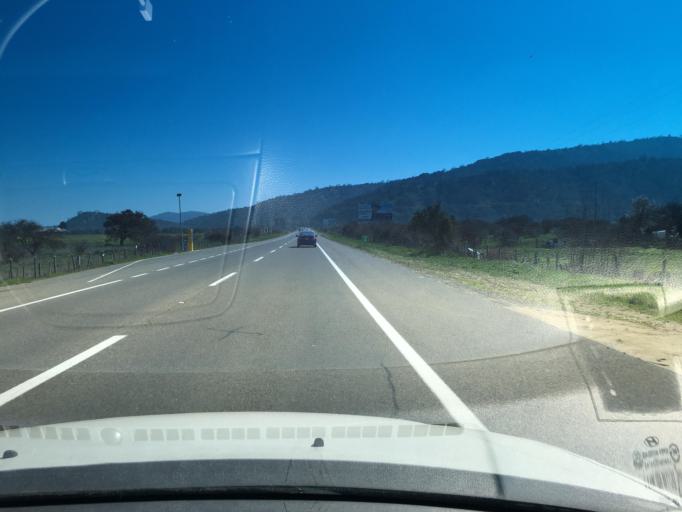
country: CL
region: Valparaiso
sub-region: San Antonio Province
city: El Tabo
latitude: -33.3901
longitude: -71.4485
